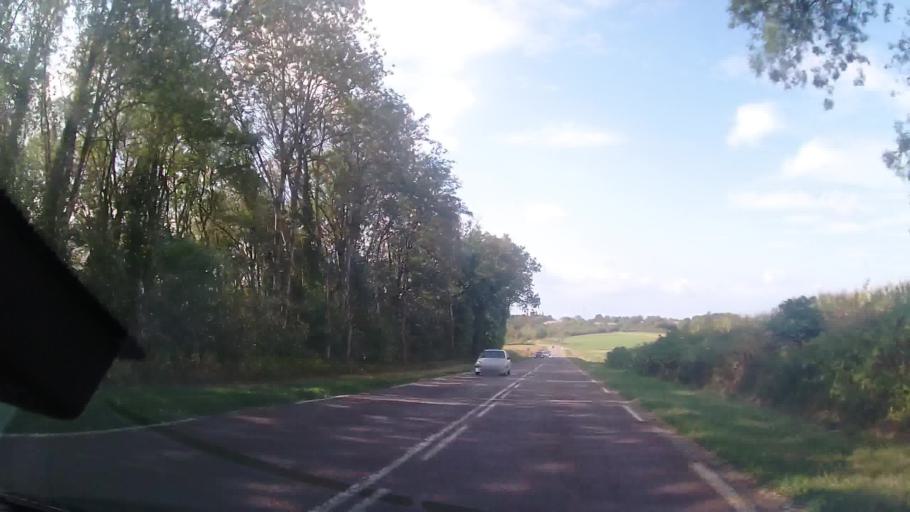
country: FR
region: Franche-Comte
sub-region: Departement du Jura
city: Perrigny
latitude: 46.6406
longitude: 5.5850
